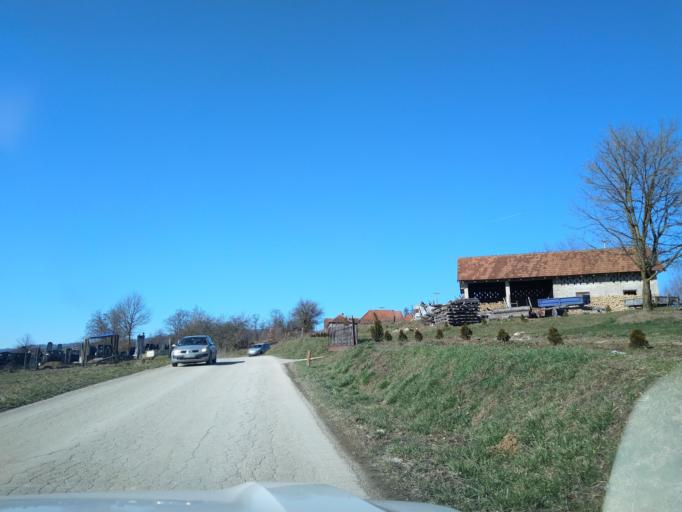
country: RS
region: Central Serbia
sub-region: Zlatiborski Okrug
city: Kosjeric
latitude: 43.9356
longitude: 19.8831
